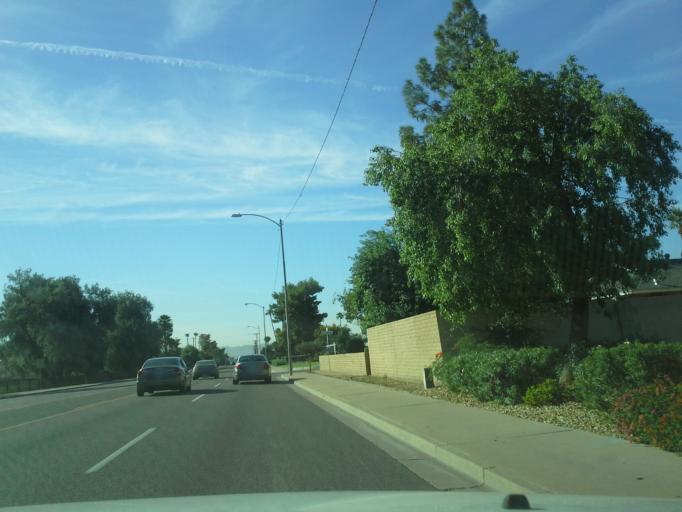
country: US
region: Arizona
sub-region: Maricopa County
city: Phoenix
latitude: 33.4789
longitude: -112.1005
